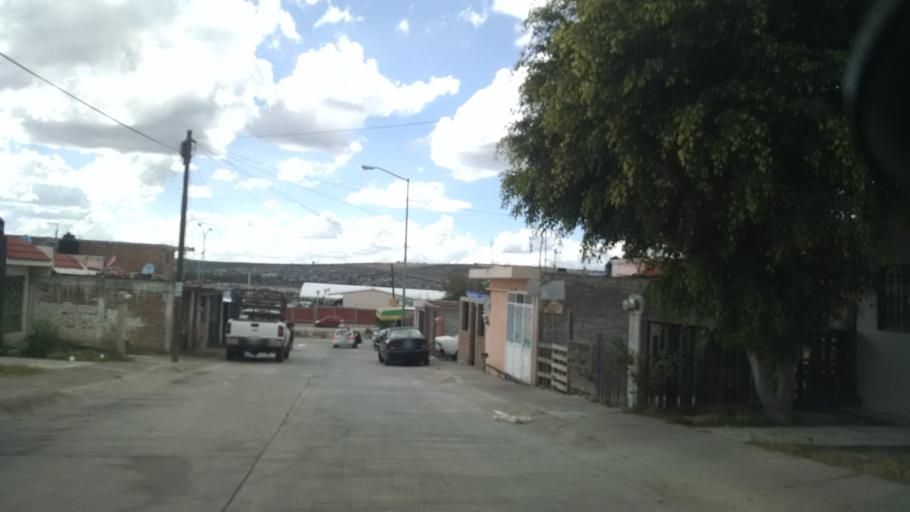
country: MX
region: Guanajuato
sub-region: Leon
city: La Ermita
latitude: 21.1540
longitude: -101.7360
